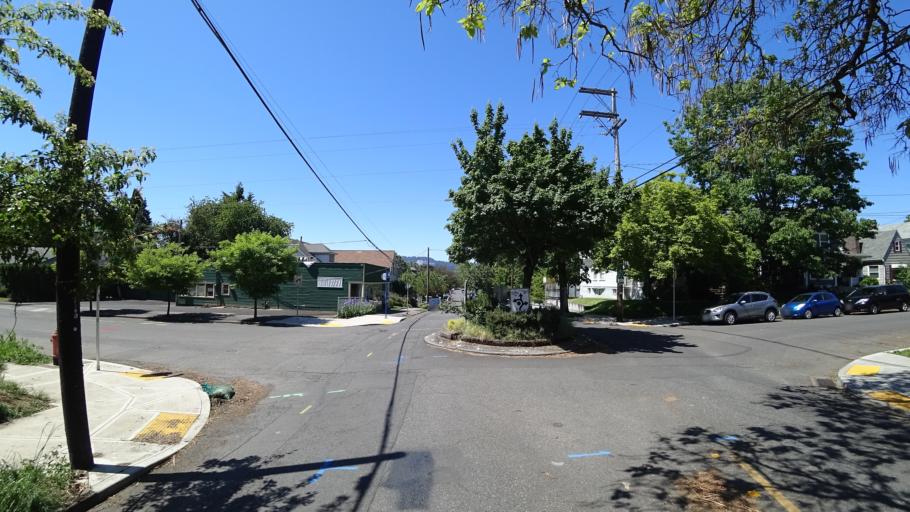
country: US
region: Oregon
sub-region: Multnomah County
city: Portland
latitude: 45.5034
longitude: -122.6425
